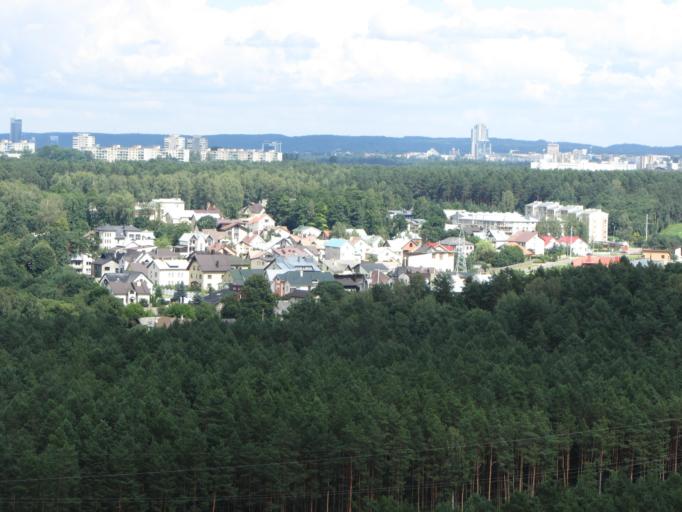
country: LT
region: Vilnius County
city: Lazdynai
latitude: 54.6601
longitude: 25.1743
